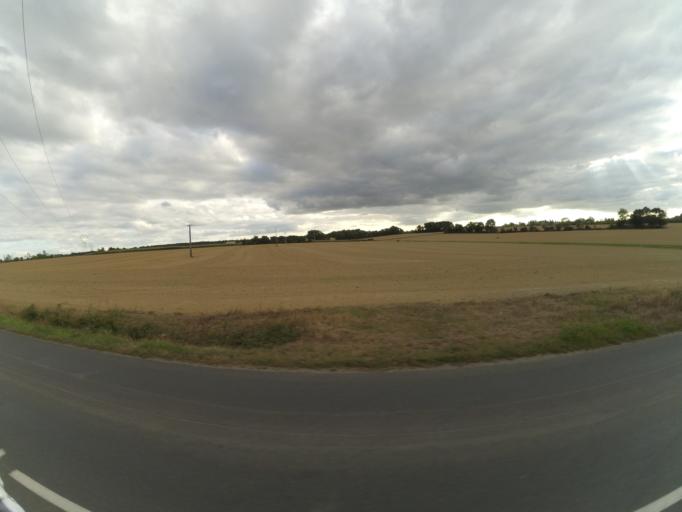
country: FR
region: Pays de la Loire
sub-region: Departement de la Vendee
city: Saint-Andre-Treize-Voies
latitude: 46.9218
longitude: -1.3932
